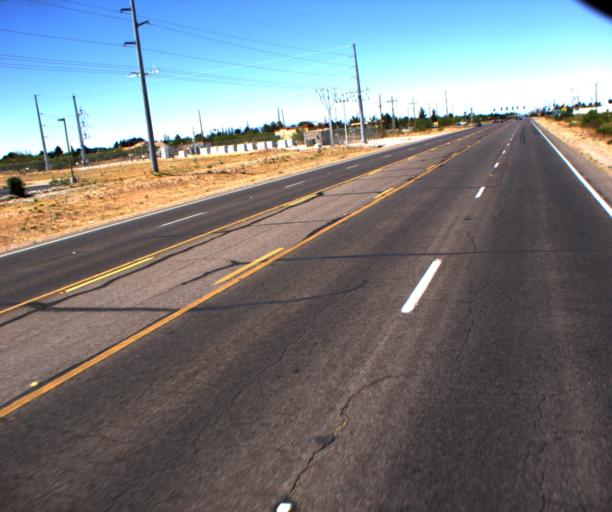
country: US
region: Arizona
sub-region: Cochise County
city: Sierra Vista Southeast
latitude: 31.4644
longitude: -110.2574
